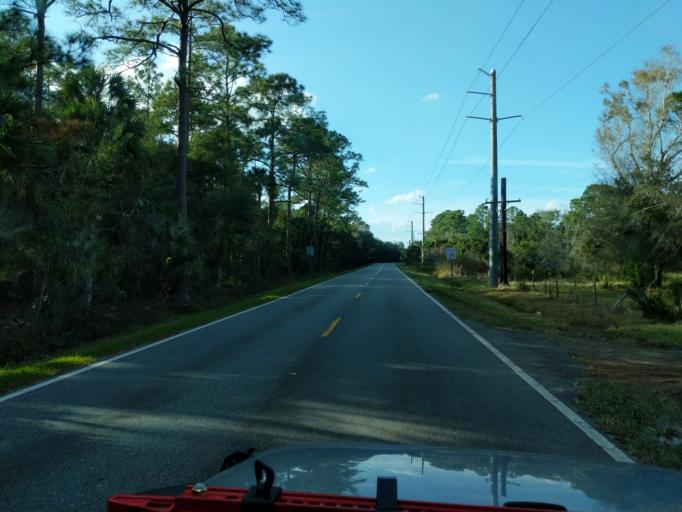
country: US
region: Florida
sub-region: Seminole County
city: Geneva
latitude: 28.7777
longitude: -81.1627
